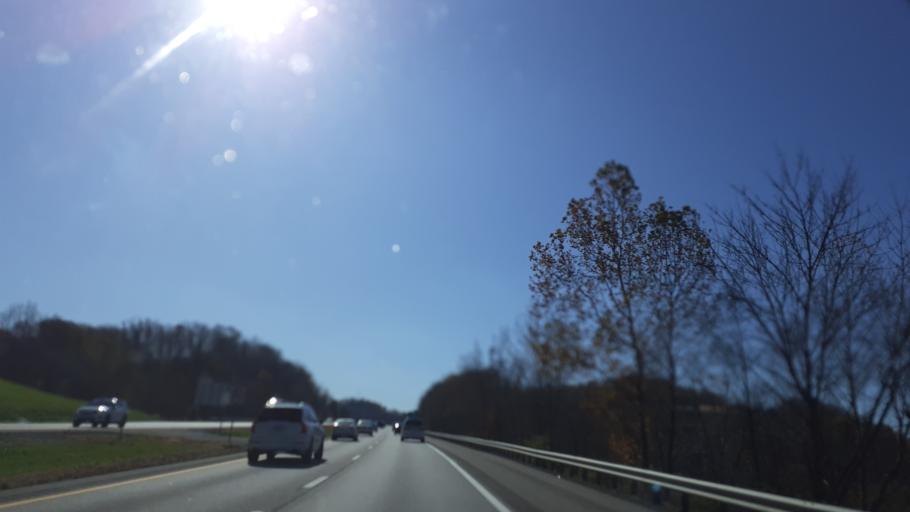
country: US
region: West Virginia
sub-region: Monongalia County
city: Brookhaven
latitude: 39.6243
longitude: -79.9089
